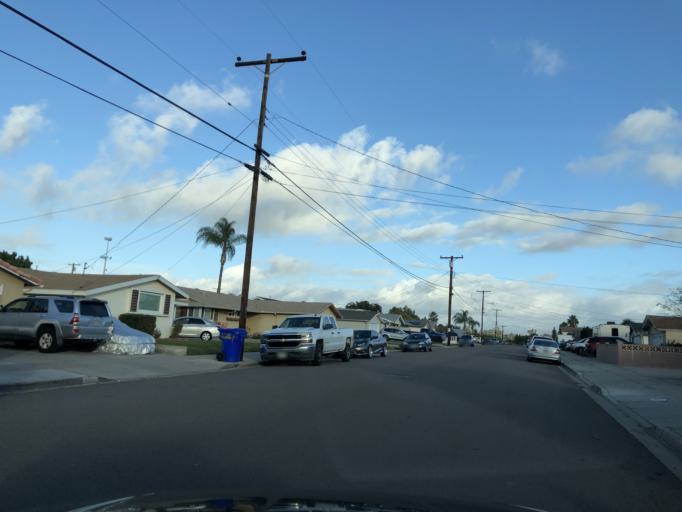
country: US
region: California
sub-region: San Diego County
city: La Jolla
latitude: 32.8182
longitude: -117.1753
